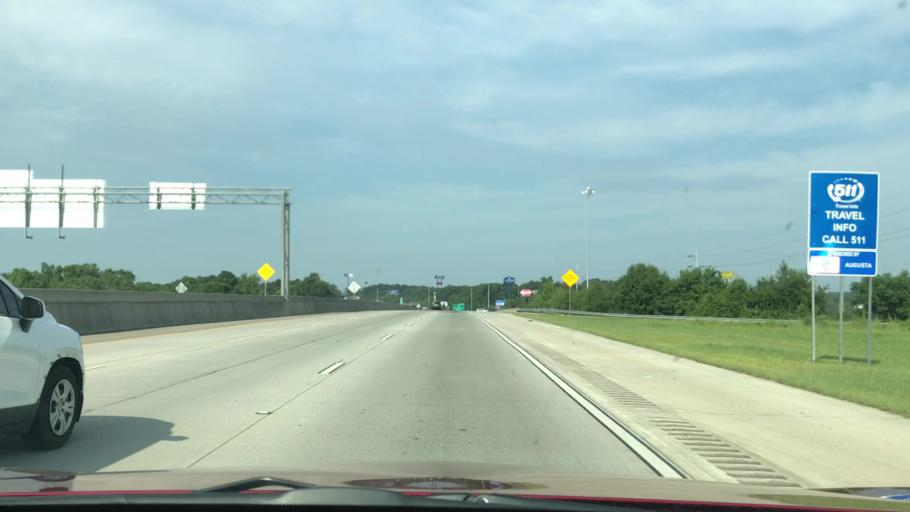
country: US
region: Georgia
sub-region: Columbia County
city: Martinez
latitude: 33.5225
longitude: -82.0294
